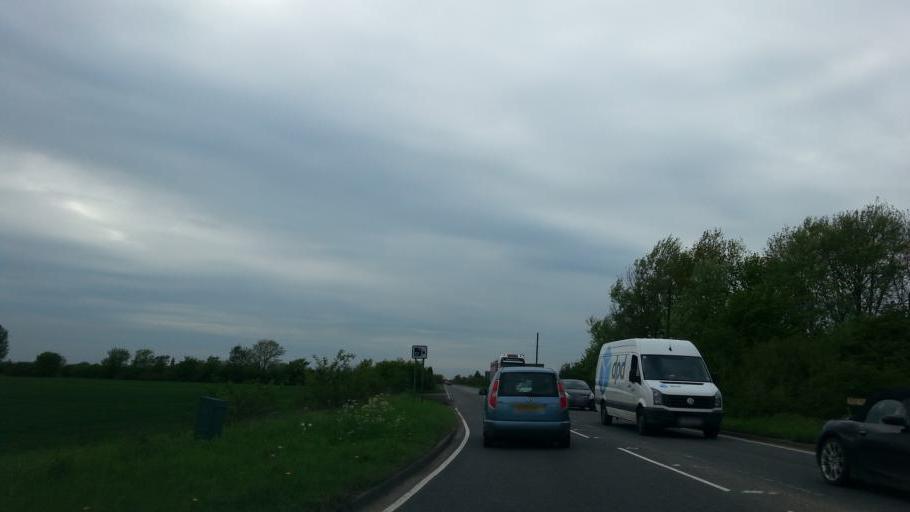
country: GB
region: England
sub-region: Cambridgeshire
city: March
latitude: 52.5235
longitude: 0.0824
